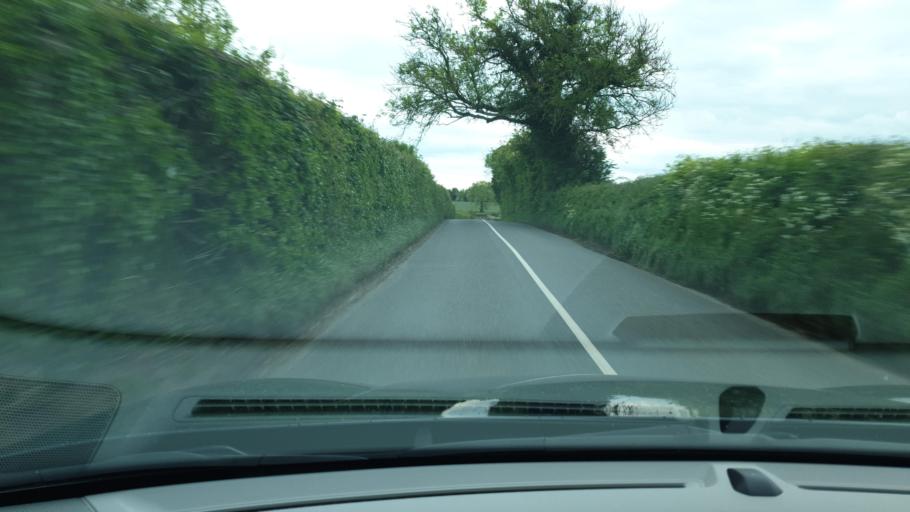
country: IE
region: Leinster
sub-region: An Mhi
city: Ashbourne
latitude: 53.5608
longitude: -6.3376
